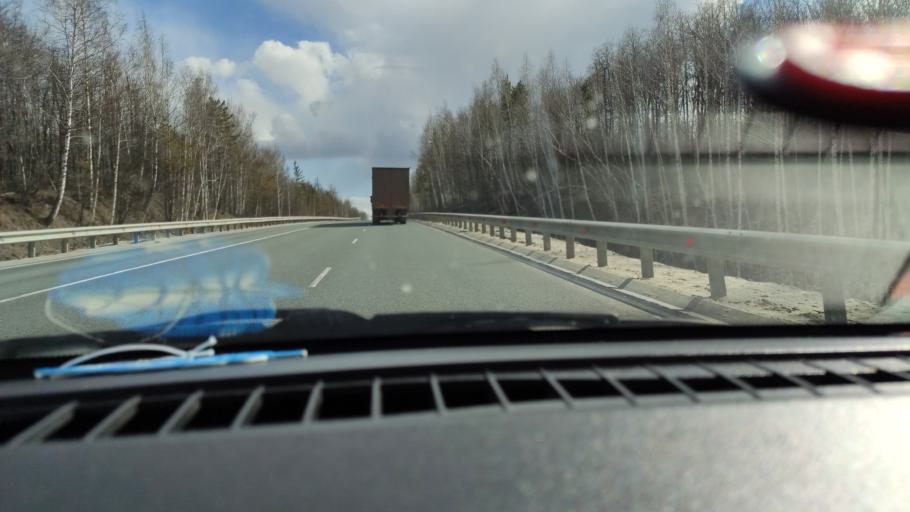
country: RU
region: Saratov
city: Khvalynsk
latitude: 52.4952
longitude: 48.0144
